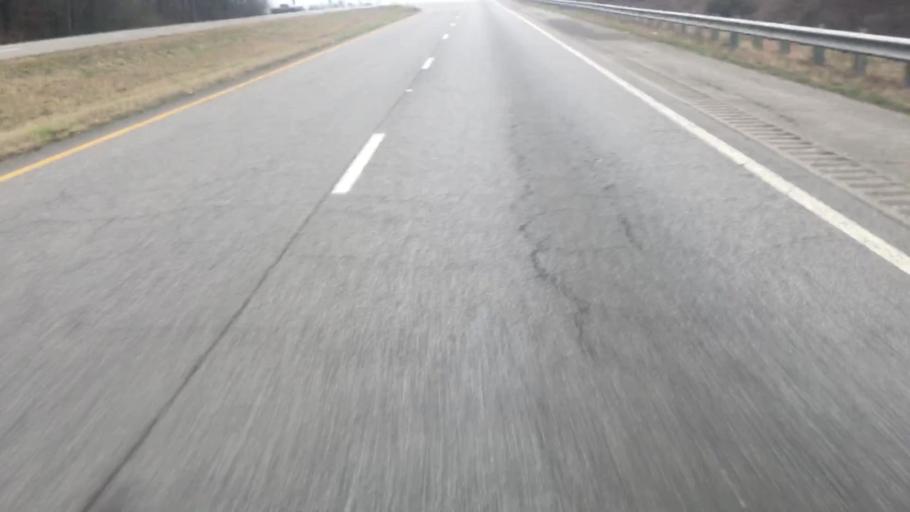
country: US
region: Alabama
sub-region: Jefferson County
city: Graysville
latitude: 33.6524
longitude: -86.9745
